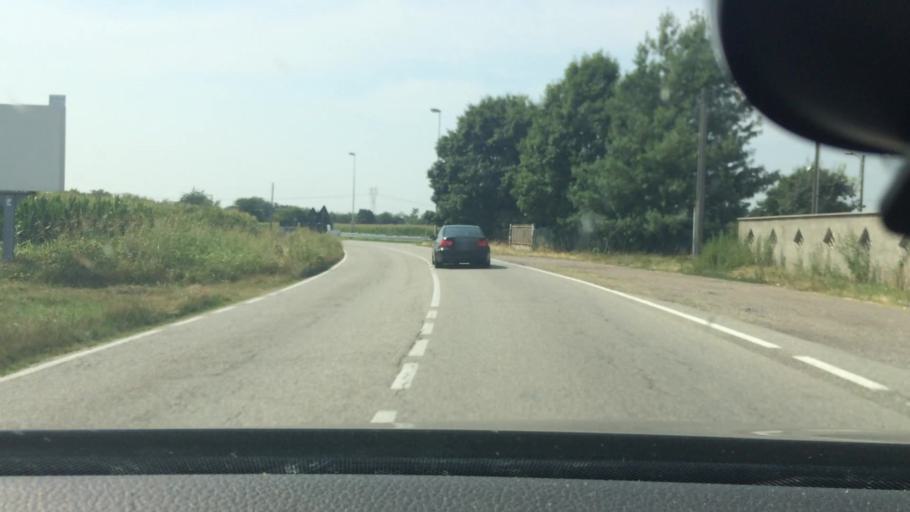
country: IT
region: Lombardy
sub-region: Citta metropolitana di Milano
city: Casorezzo
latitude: 45.5375
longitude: 8.8954
